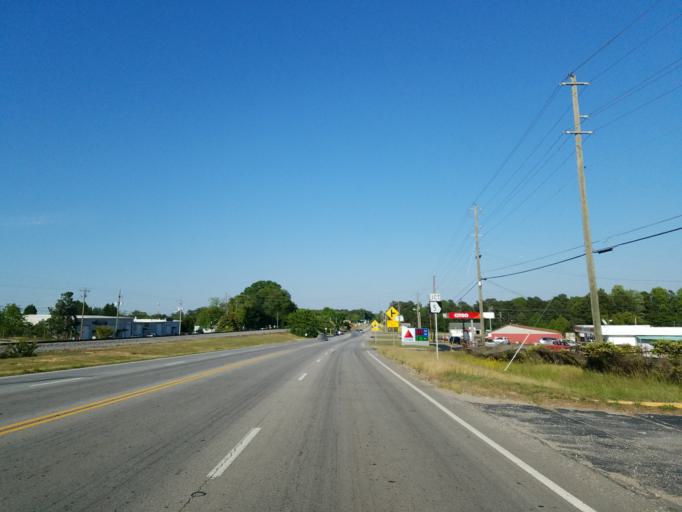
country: US
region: Georgia
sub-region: Douglas County
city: Douglasville
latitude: 33.7420
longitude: -84.7796
